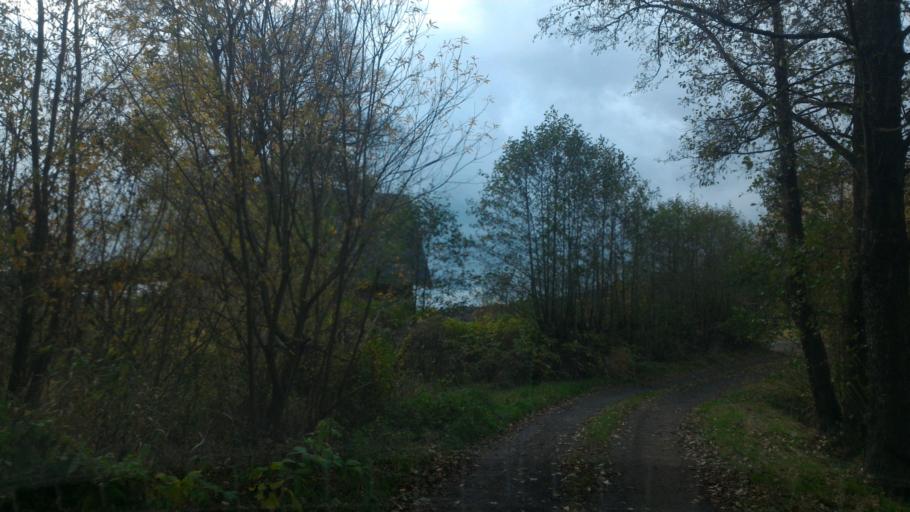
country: CZ
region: Ustecky
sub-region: Okres Decin
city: Krasna Lipa
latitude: 50.8830
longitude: 14.5408
